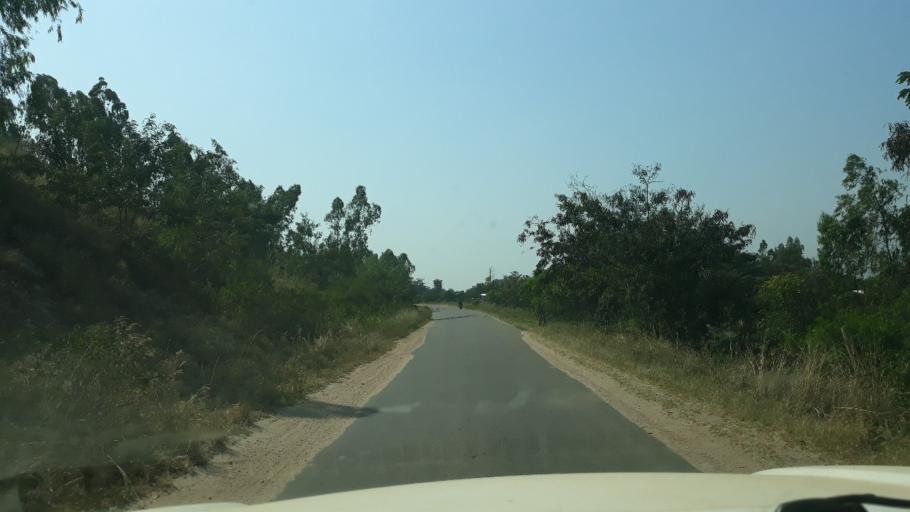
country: CD
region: South Kivu
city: Uvira
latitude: -3.2883
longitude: 29.1609
